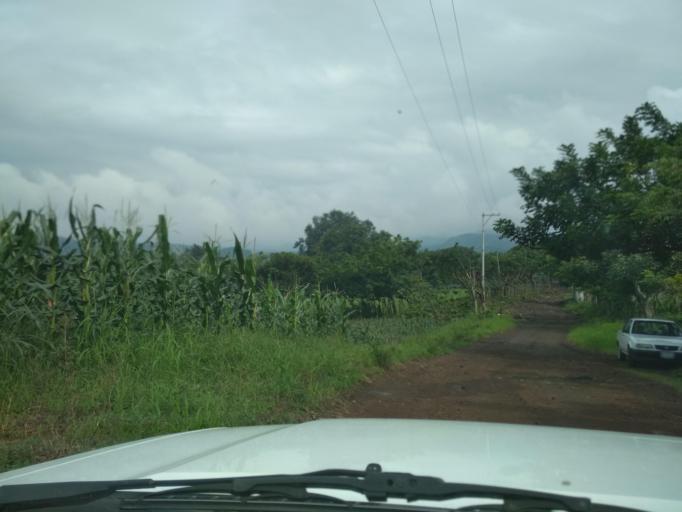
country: MX
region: Veracruz
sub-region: San Andres Tuxtla
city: Matacapan
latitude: 18.4395
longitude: -95.1496
